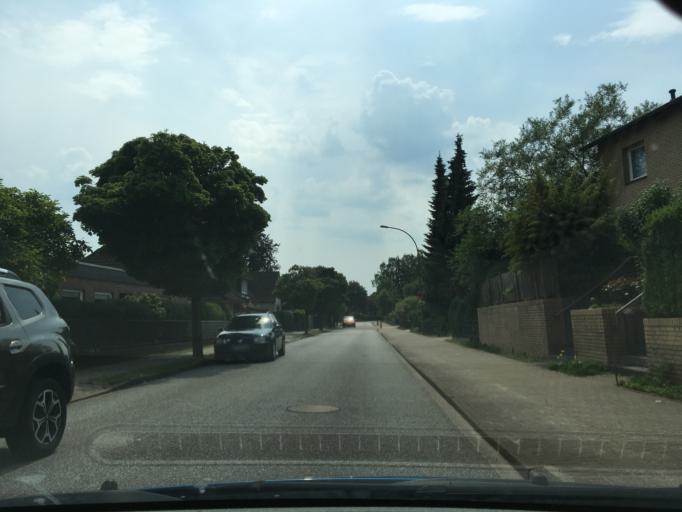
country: DE
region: Lower Saxony
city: Buchholz in der Nordheide
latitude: 53.3342
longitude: 9.8866
